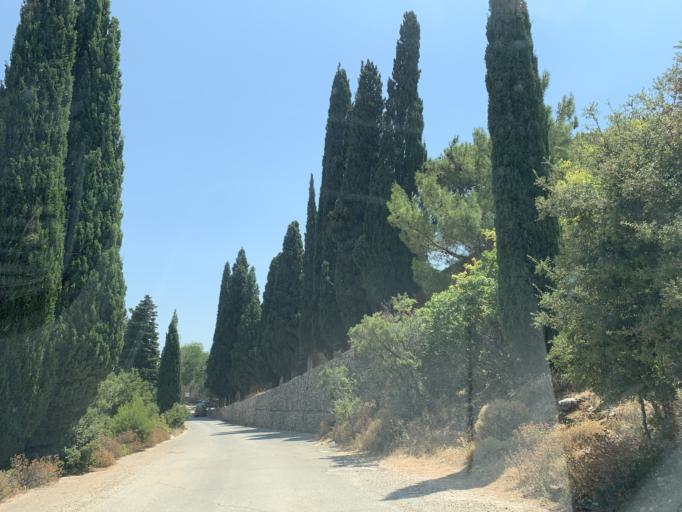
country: GR
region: North Aegean
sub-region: Chios
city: Chios
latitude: 38.3748
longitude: 26.0547
